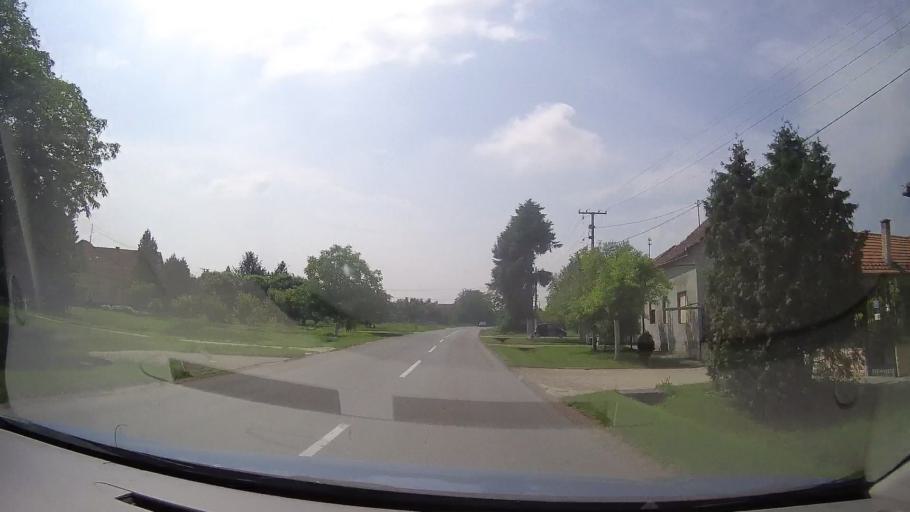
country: RS
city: Padina
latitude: 45.1278
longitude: 20.7210
